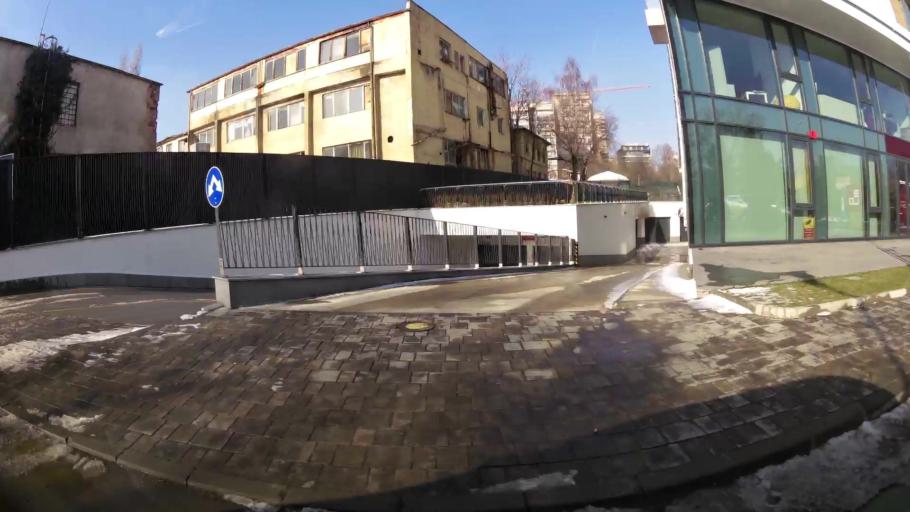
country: BG
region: Sofia-Capital
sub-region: Stolichna Obshtina
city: Sofia
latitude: 42.6662
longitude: 23.3440
